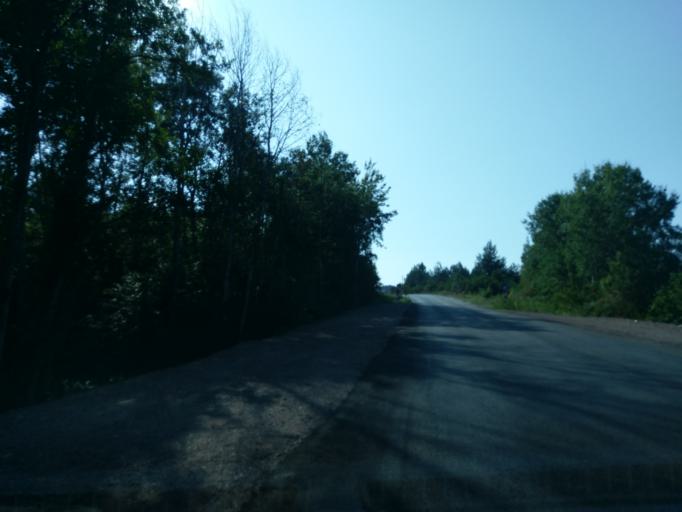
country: TR
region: Sinop
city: Yenikonak
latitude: 41.9433
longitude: 34.7314
